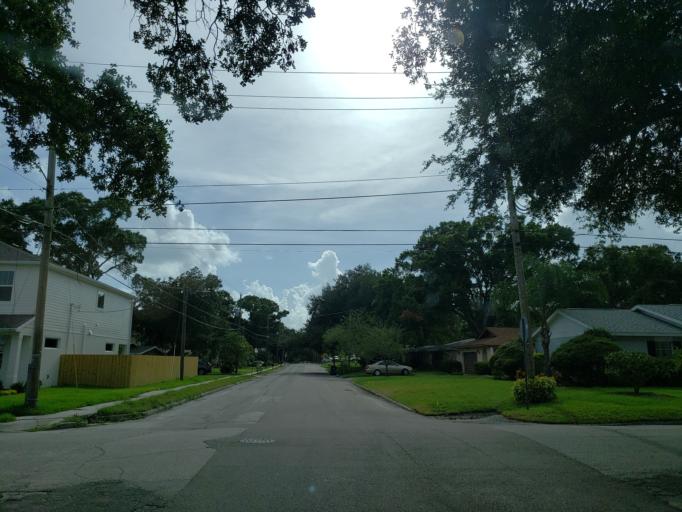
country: US
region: Florida
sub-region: Hillsborough County
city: Tampa
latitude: 27.9467
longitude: -82.5180
